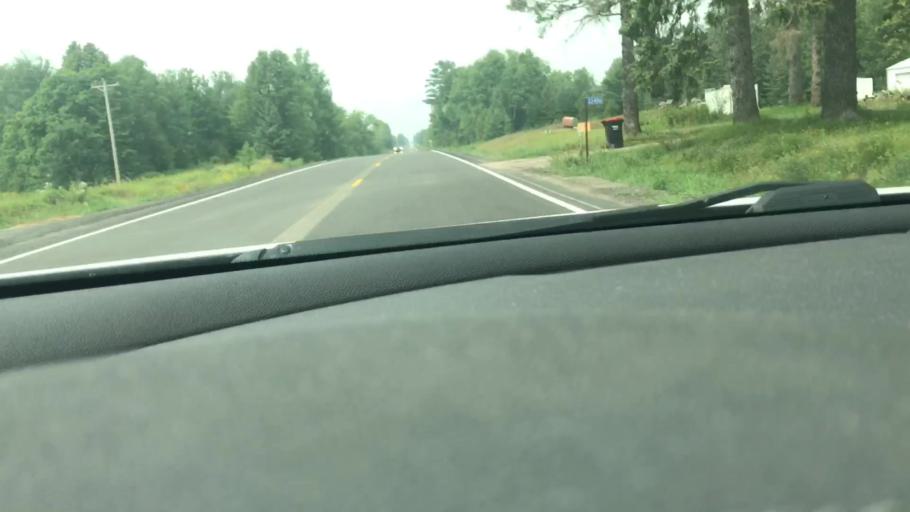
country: US
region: Minnesota
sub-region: Itasca County
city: Cohasset
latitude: 47.3596
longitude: -93.8607
